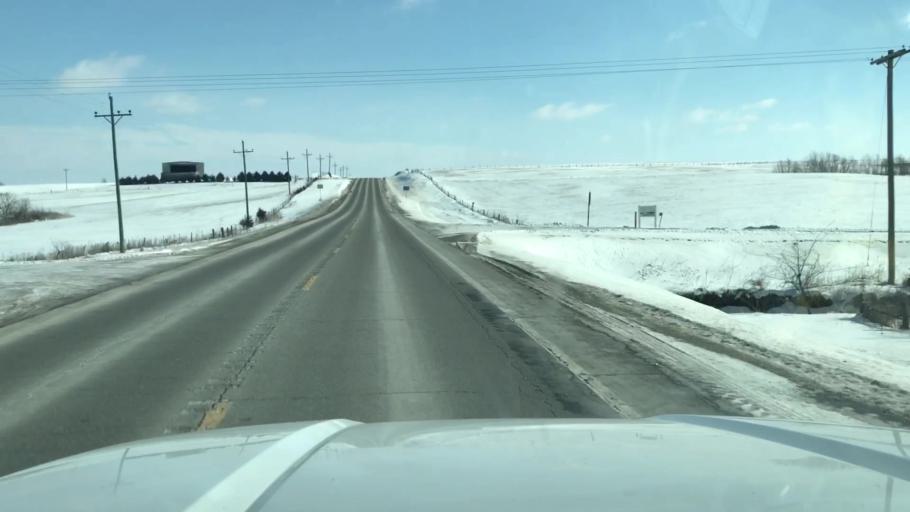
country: US
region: Missouri
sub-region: Nodaway County
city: Maryville
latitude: 40.3440
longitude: -94.7417
